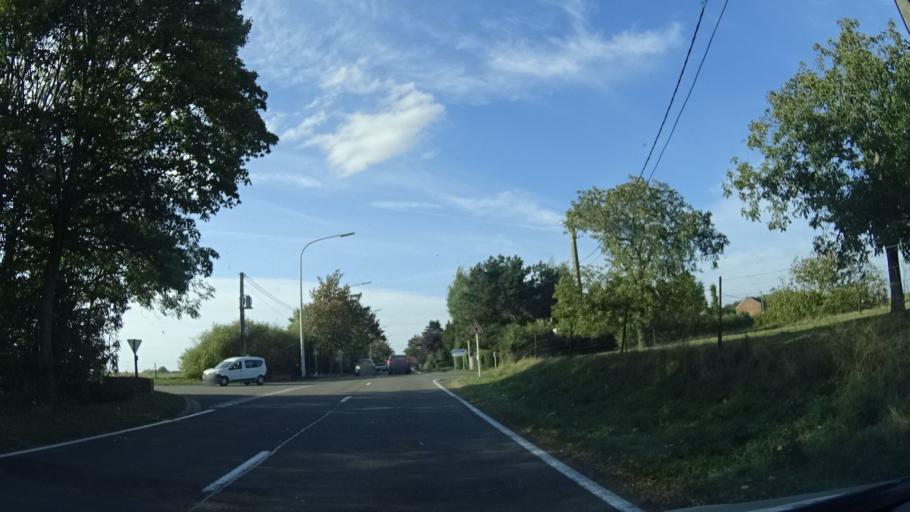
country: BE
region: Wallonia
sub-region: Province du Hainaut
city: Beaumont
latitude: 50.2435
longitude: 4.2330
